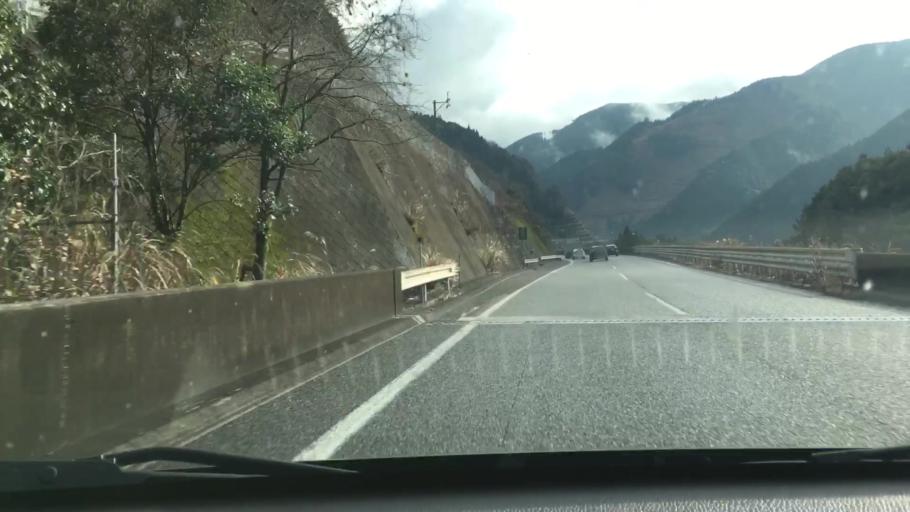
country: JP
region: Kumamoto
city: Yatsushiro
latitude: 32.4089
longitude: 130.6968
